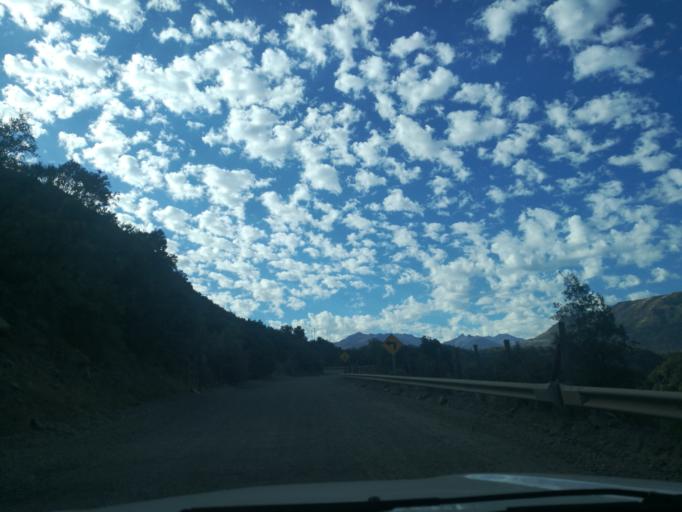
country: CL
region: O'Higgins
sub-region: Provincia de Cachapoal
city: Machali
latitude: -34.2826
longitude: -70.4419
